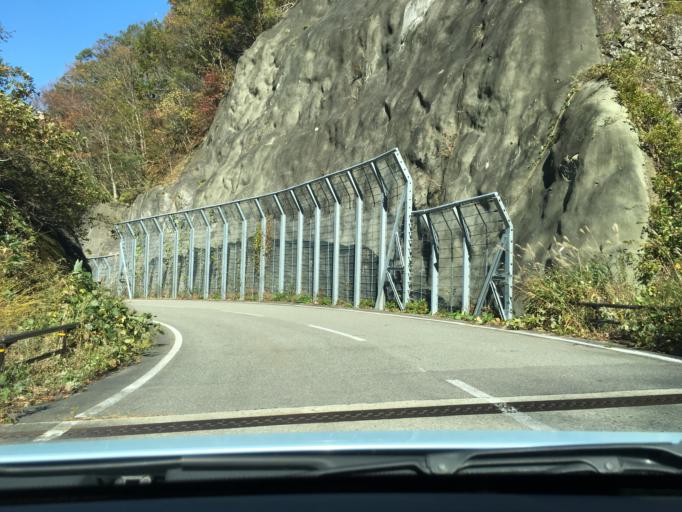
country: JP
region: Fukushima
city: Inawashiro
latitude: 37.4653
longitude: 139.9684
